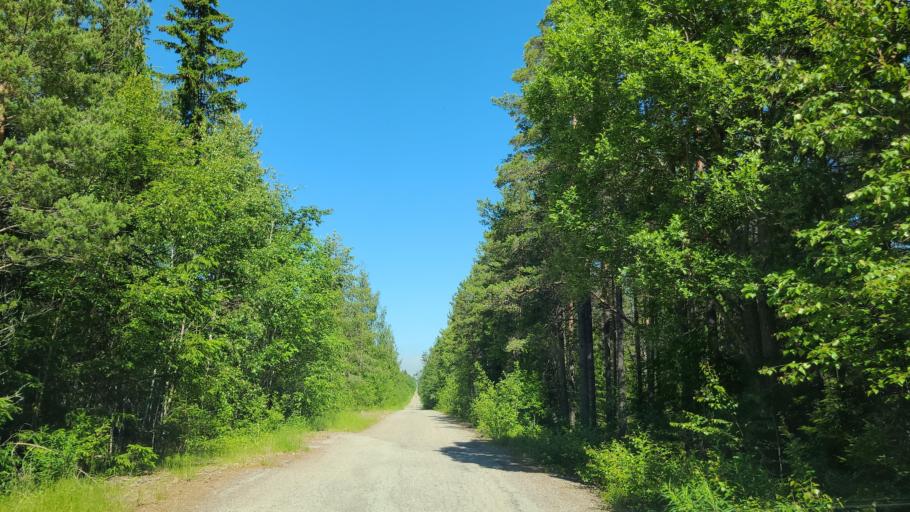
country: SE
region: Vaesternorrland
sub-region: OErnskoeldsviks Kommun
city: Husum
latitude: 63.4179
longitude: 19.2218
